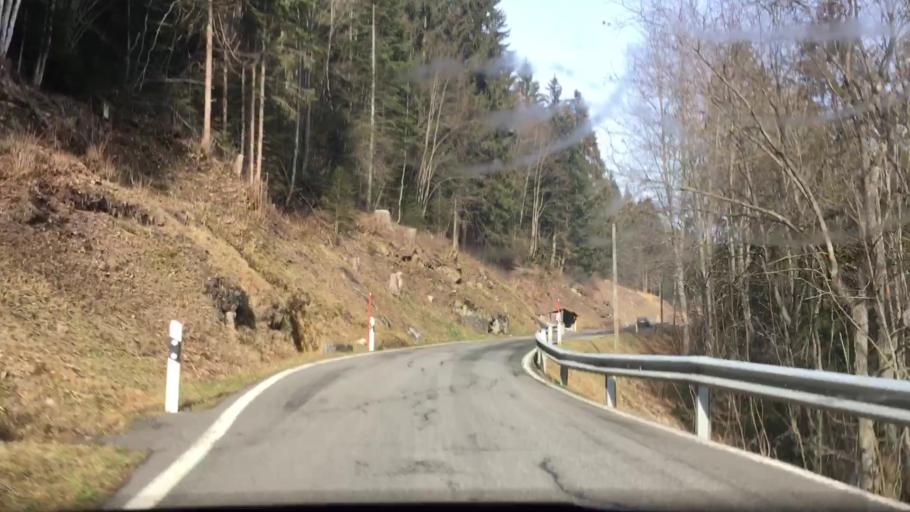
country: CH
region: Valais
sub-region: Monthey District
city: Troistorrents
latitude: 46.2257
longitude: 6.9009
